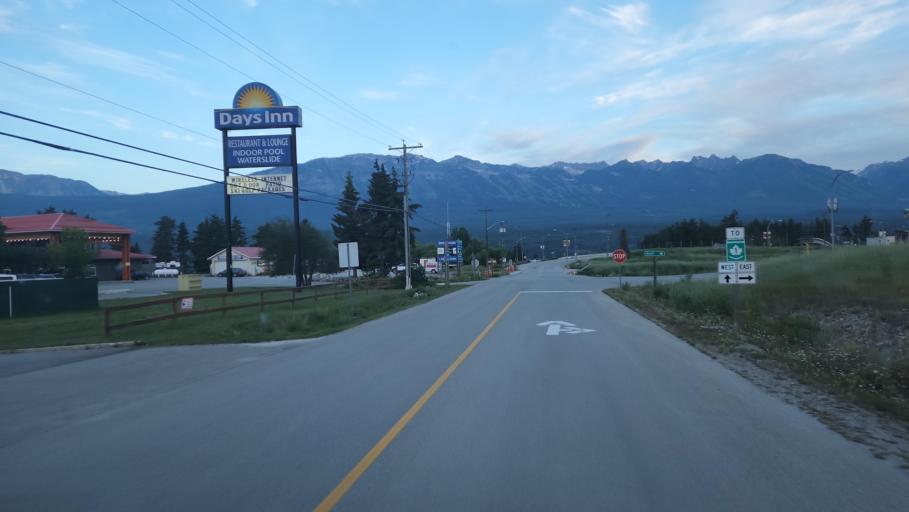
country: CA
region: British Columbia
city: Golden
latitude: 51.3013
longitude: -116.9501
